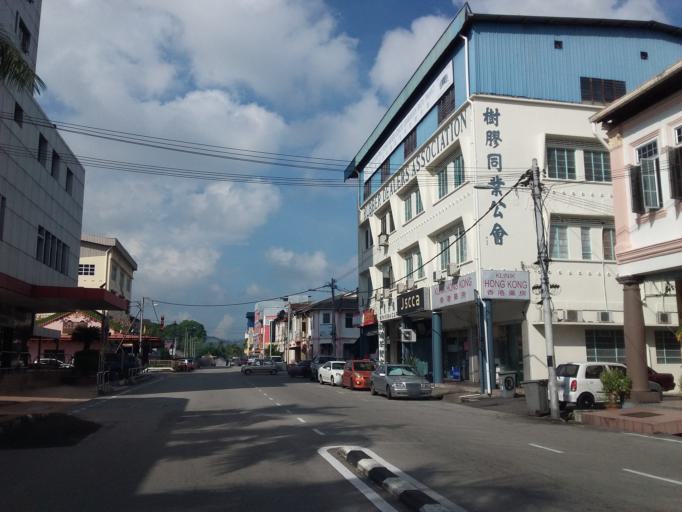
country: MY
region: Johor
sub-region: Daerah Batu Pahat
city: Batu Pahat
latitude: 1.8496
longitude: 102.9279
